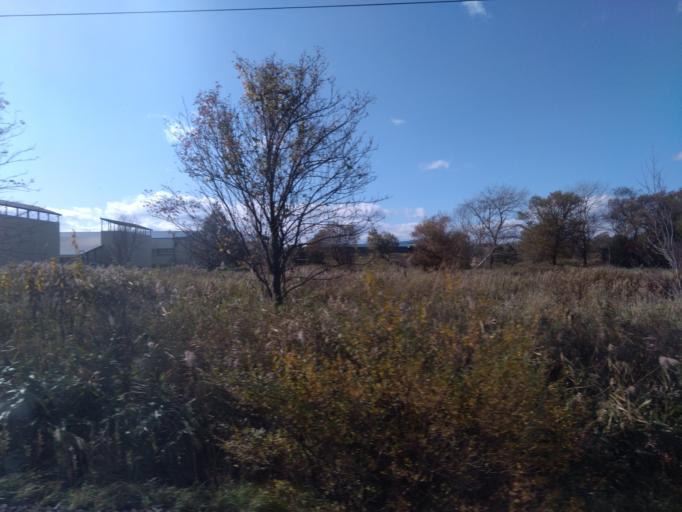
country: JP
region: Hokkaido
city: Kitahiroshima
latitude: 42.9576
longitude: 141.5694
